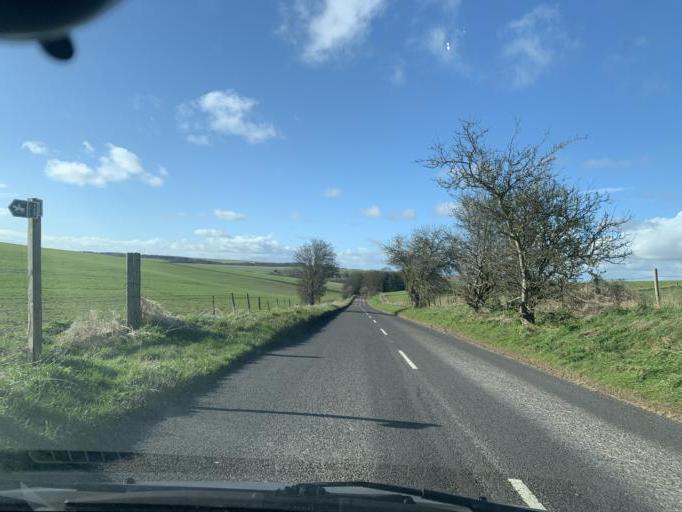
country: GB
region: England
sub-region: Wiltshire
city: Stockton
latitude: 51.1903
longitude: -2.0035
